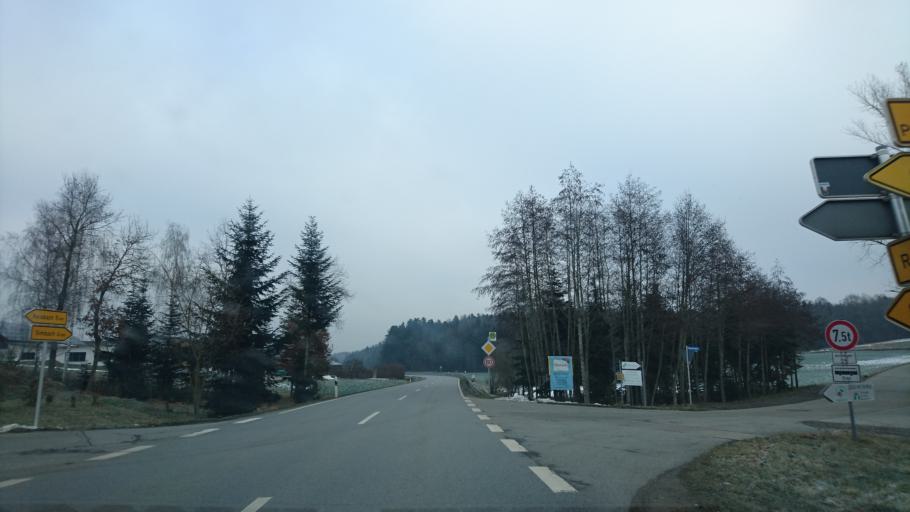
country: DE
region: Bavaria
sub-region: Lower Bavaria
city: Ruhstorf
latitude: 48.5618
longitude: 12.6840
